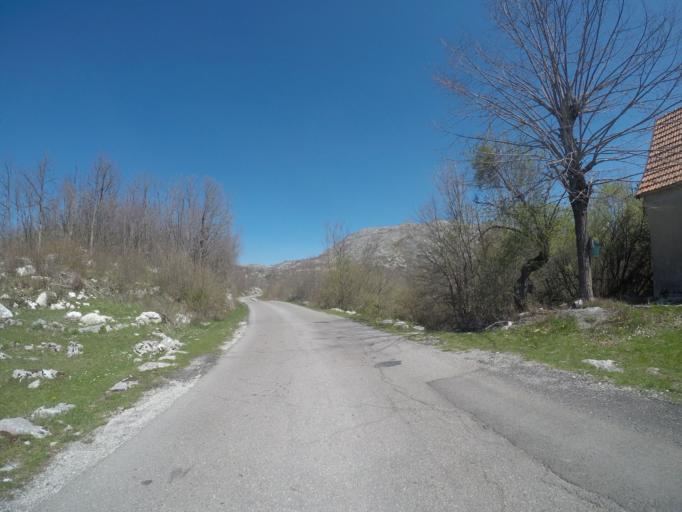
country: ME
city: Dobrota
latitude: 42.4909
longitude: 18.8684
